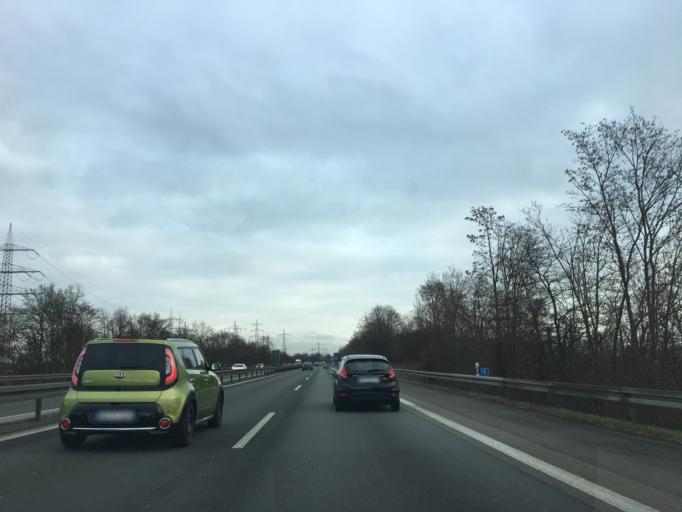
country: DE
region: North Rhine-Westphalia
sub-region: Regierungsbezirk Koln
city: Troisdorf
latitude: 50.7960
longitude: 7.1596
